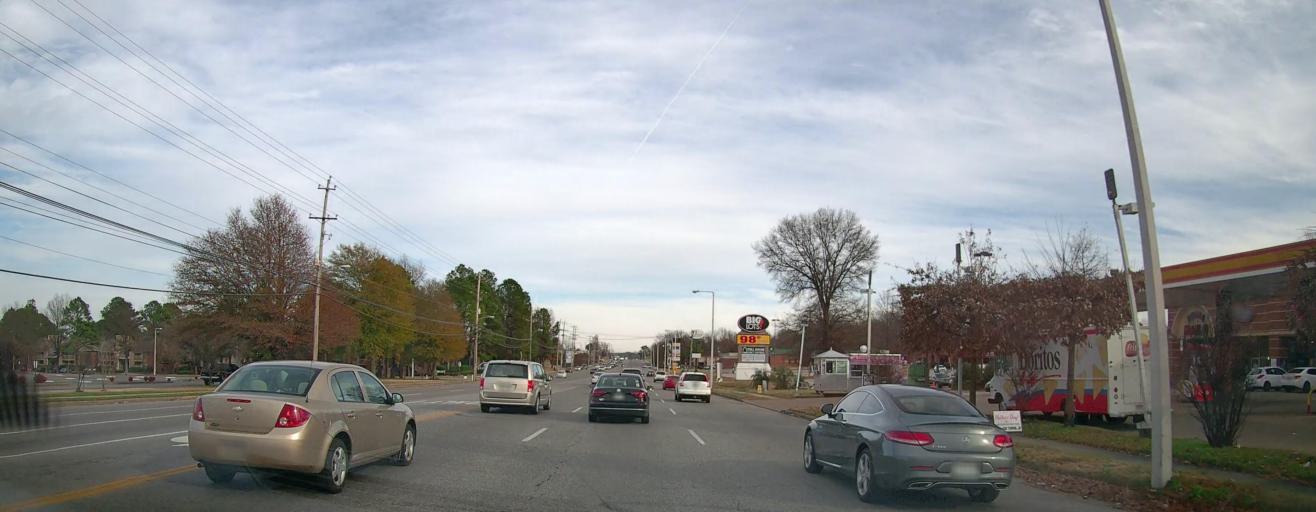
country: US
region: Tennessee
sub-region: Shelby County
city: Germantown
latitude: 35.0494
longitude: -89.8386
